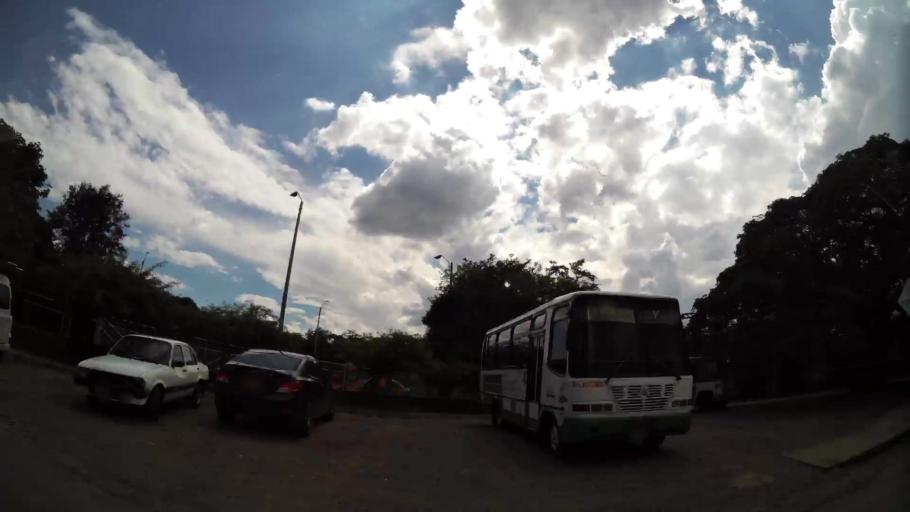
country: CO
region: Valle del Cauca
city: Cali
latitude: 3.4059
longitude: -76.5198
